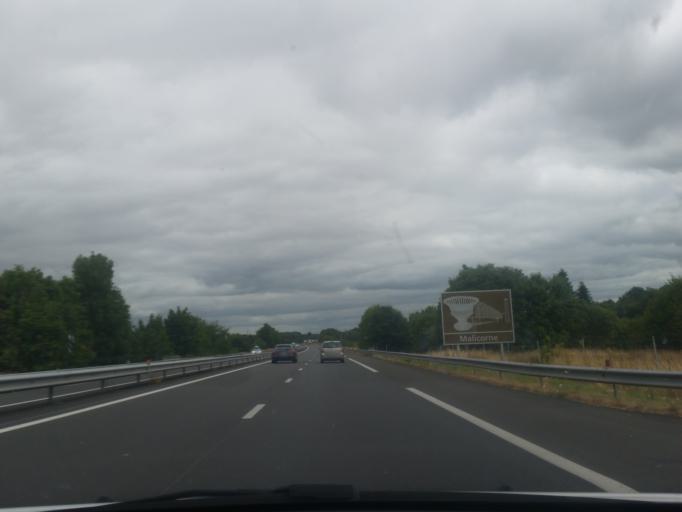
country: FR
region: Pays de la Loire
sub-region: Departement de la Sarthe
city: Vion
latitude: 47.7565
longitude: -0.2336
